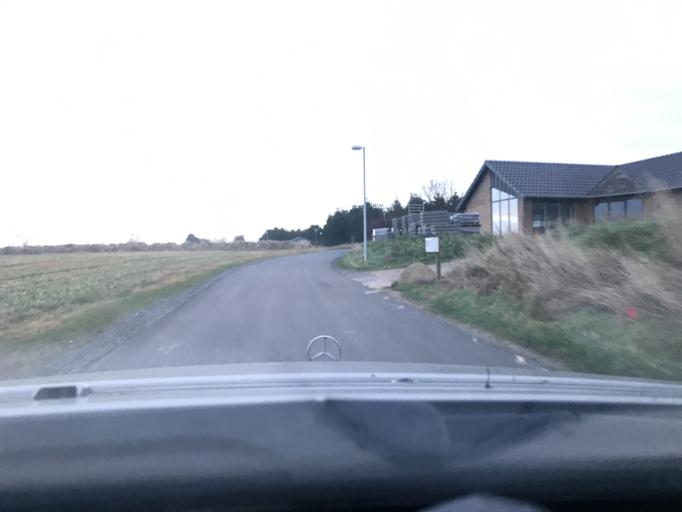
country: DK
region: South Denmark
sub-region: Sonderborg Kommune
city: Nordborg
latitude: 55.0547
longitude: 9.7032
